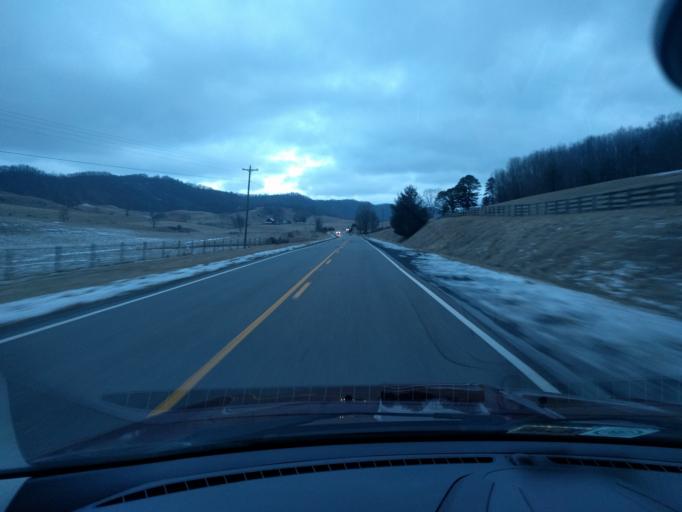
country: US
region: Virginia
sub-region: Alleghany County
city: Clifton Forge
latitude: 37.9070
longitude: -79.8977
